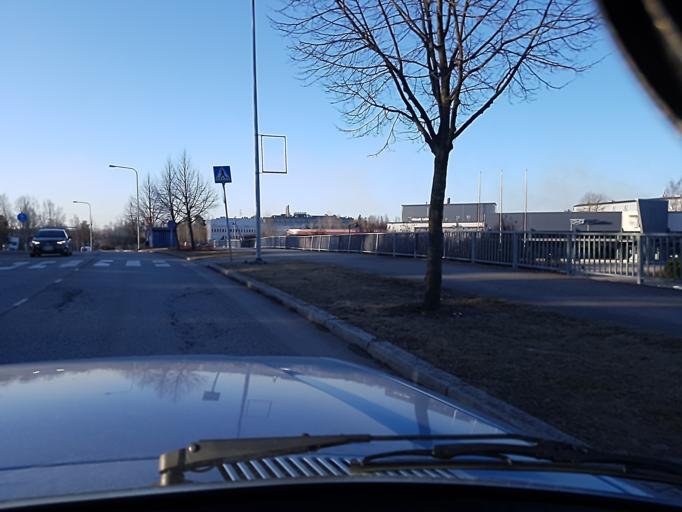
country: FI
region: Uusimaa
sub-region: Helsinki
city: Vantaa
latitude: 60.2947
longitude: 24.9894
